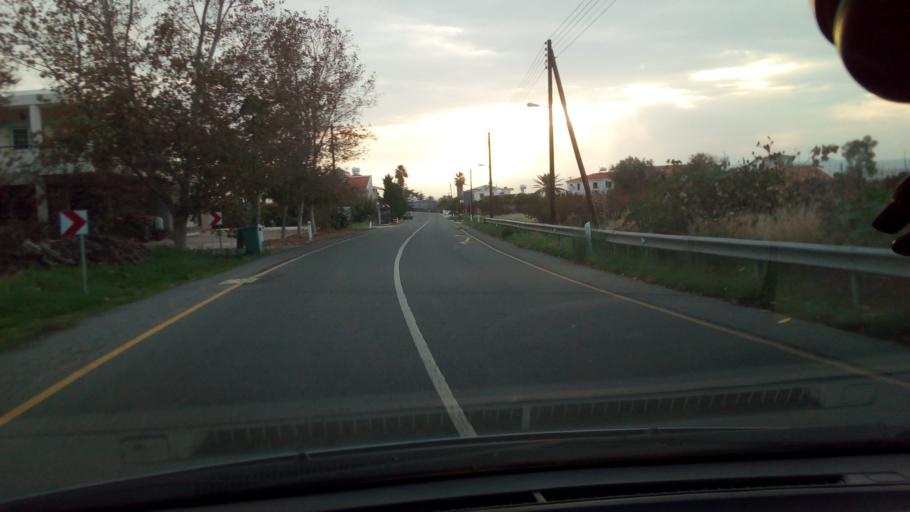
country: CY
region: Pafos
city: Polis
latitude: 35.1237
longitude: 32.5161
